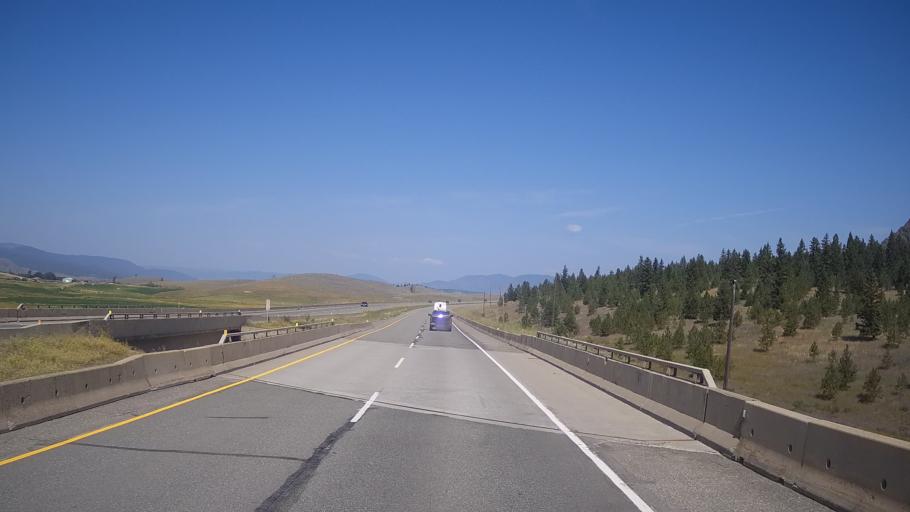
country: CA
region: British Columbia
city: Kamloops
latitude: 50.6269
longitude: -120.4764
